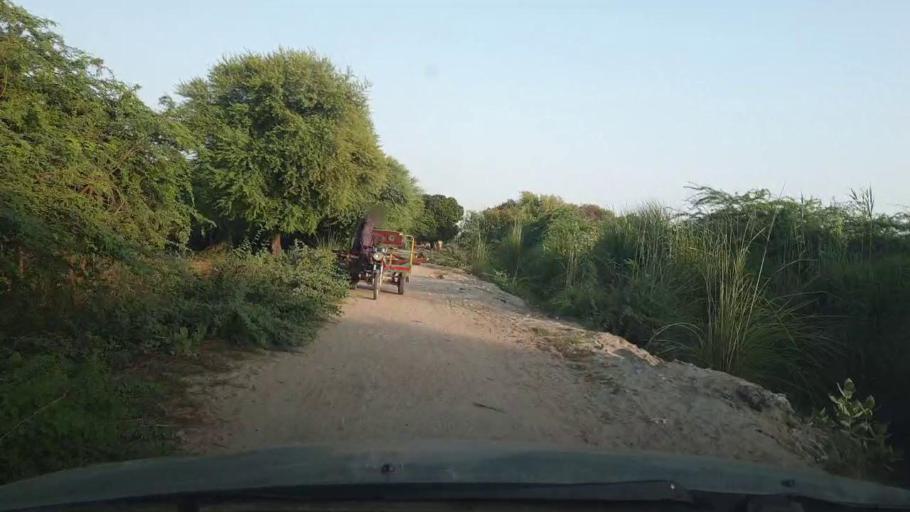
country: PK
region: Sindh
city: Tando Ghulam Ali
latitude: 25.1502
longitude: 68.9672
